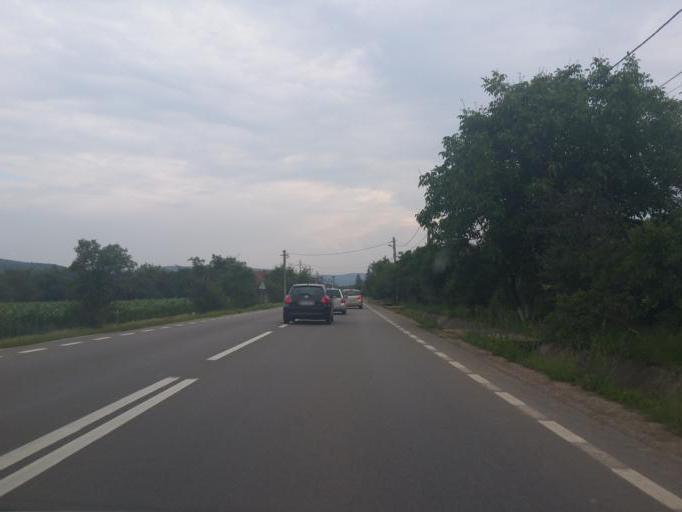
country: RO
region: Salaj
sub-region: Comuna Zimbor
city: Zimbor
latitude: 47.0096
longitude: 23.2622
